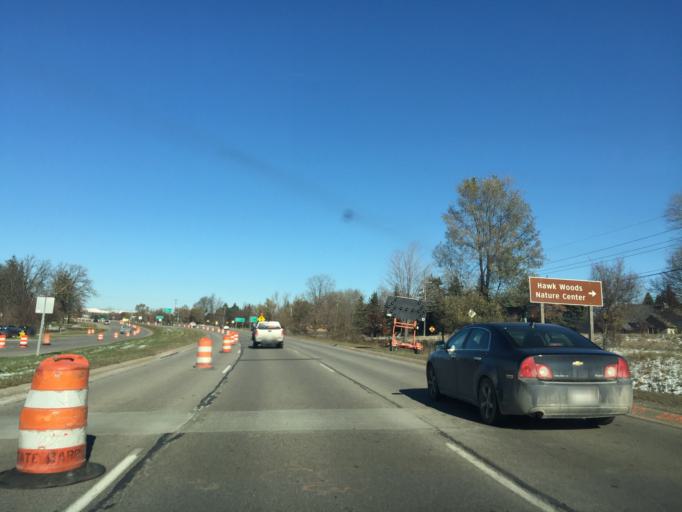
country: US
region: Michigan
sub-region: Oakland County
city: Auburn Hills
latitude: 42.6861
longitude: -83.2412
